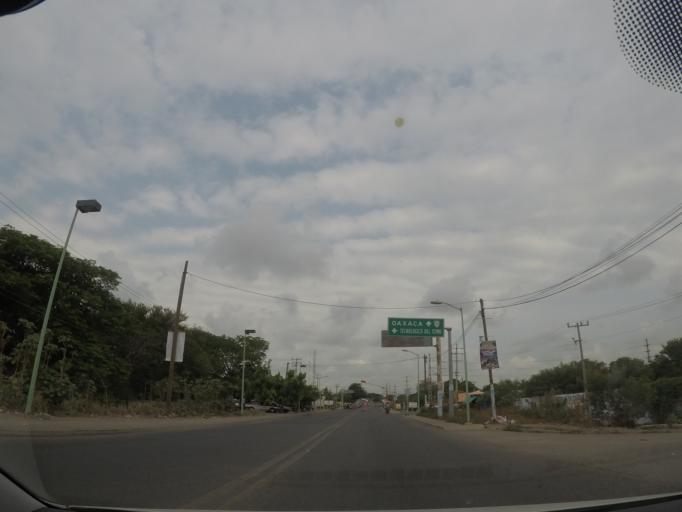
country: MX
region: Oaxaca
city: Juchitan de Zaragoza
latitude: 16.4475
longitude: -95.0155
